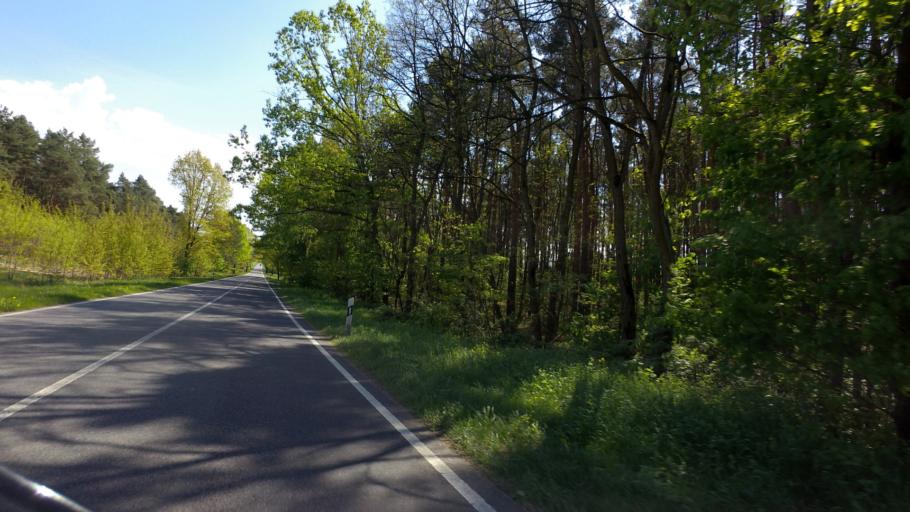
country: DE
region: Brandenburg
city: Lieberose
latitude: 51.9909
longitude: 14.2062
